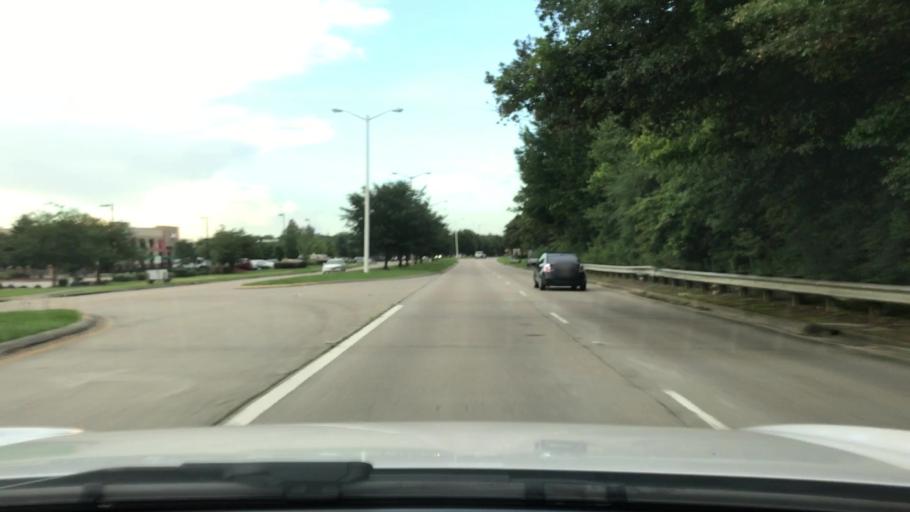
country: US
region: Louisiana
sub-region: East Baton Rouge Parish
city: Westminster
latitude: 30.4289
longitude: -91.1173
